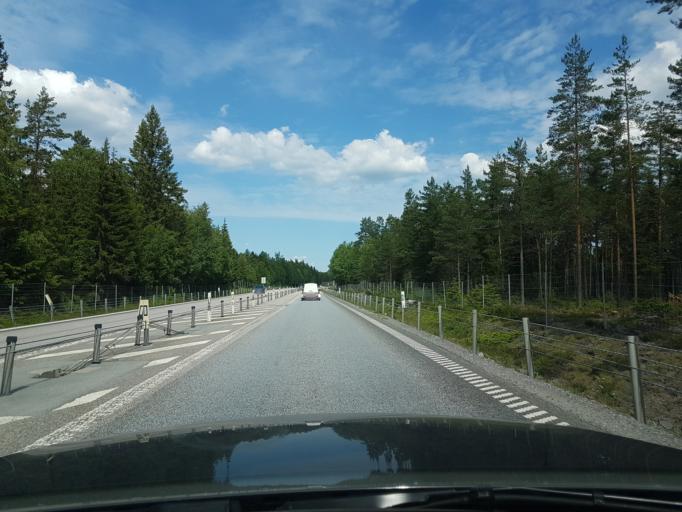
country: SE
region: Stockholm
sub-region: Osterakers Kommun
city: Akersberga
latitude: 59.6033
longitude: 18.2764
